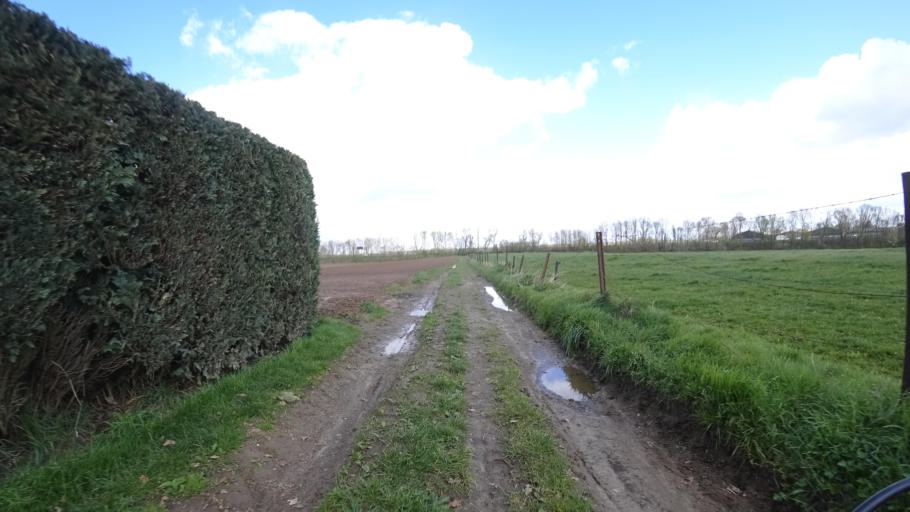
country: BE
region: Wallonia
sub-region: Province du Brabant Wallon
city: Walhain-Saint-Paul
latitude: 50.6471
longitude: 4.7072
